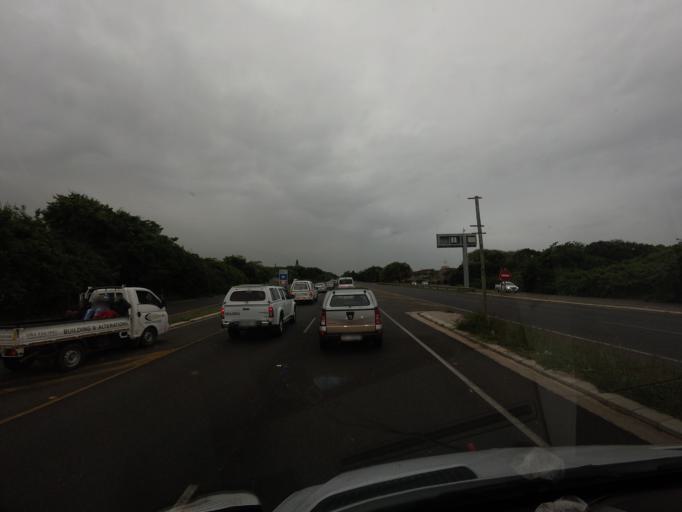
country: ZA
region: KwaZulu-Natal
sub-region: eThekwini Metropolitan Municipality
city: Durban
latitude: -29.7182
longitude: 31.0874
